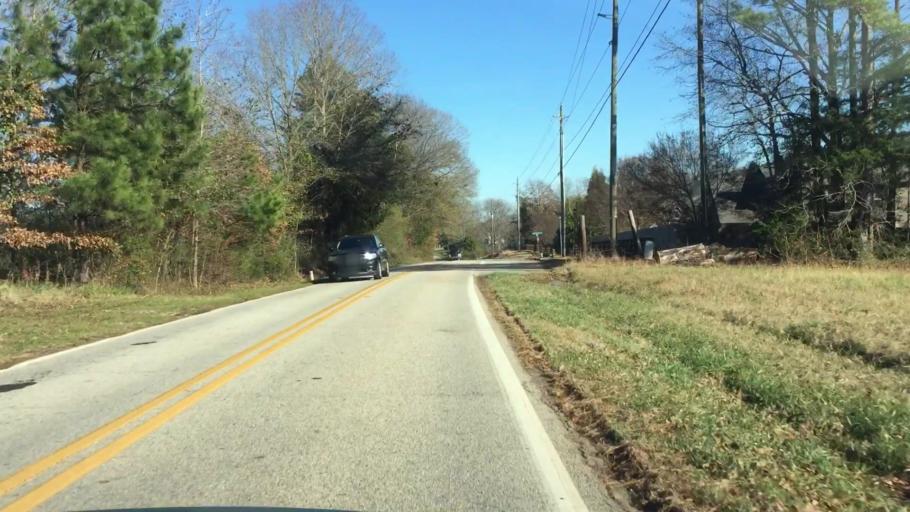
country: US
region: Georgia
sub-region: Newton County
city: Oakwood
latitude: 33.4676
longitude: -84.0070
